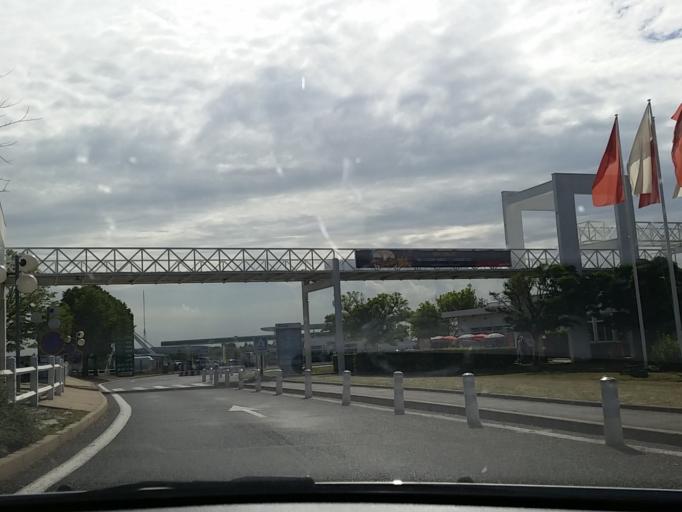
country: FR
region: Centre
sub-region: Departement du Cher
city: Orval
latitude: 46.7526
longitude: 2.4139
